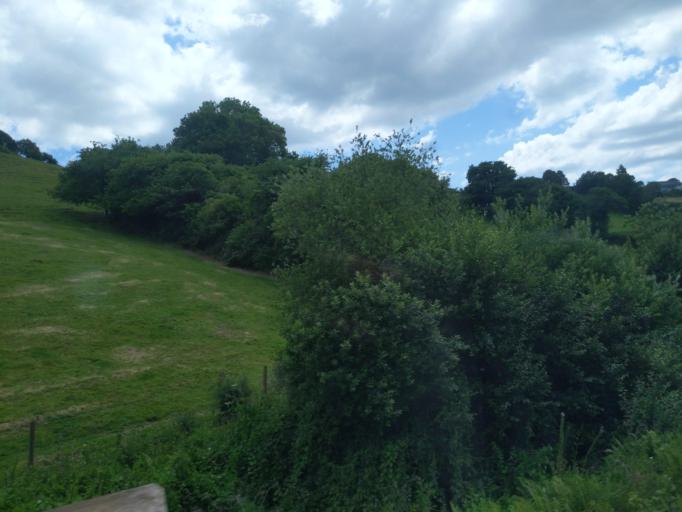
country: GB
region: England
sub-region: Cornwall
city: Par
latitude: 50.3629
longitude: -4.6910
